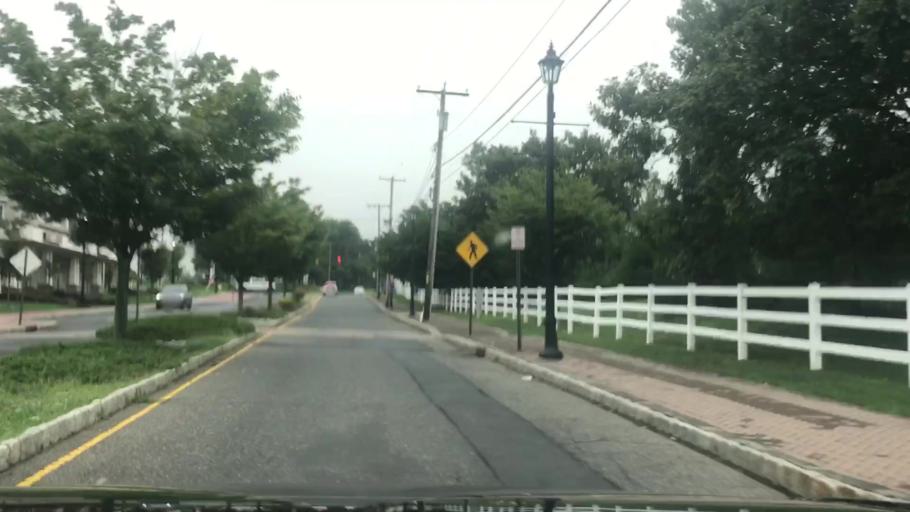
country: US
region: New Jersey
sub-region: Monmouth County
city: Oceanport
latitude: 40.3117
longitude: -74.0241
